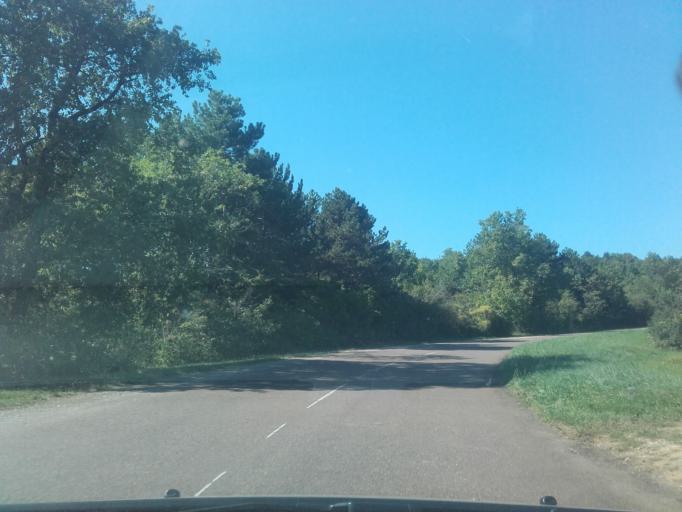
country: FR
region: Bourgogne
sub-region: Departement de la Cote-d'Or
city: Nolay
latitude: 46.9426
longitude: 4.6874
